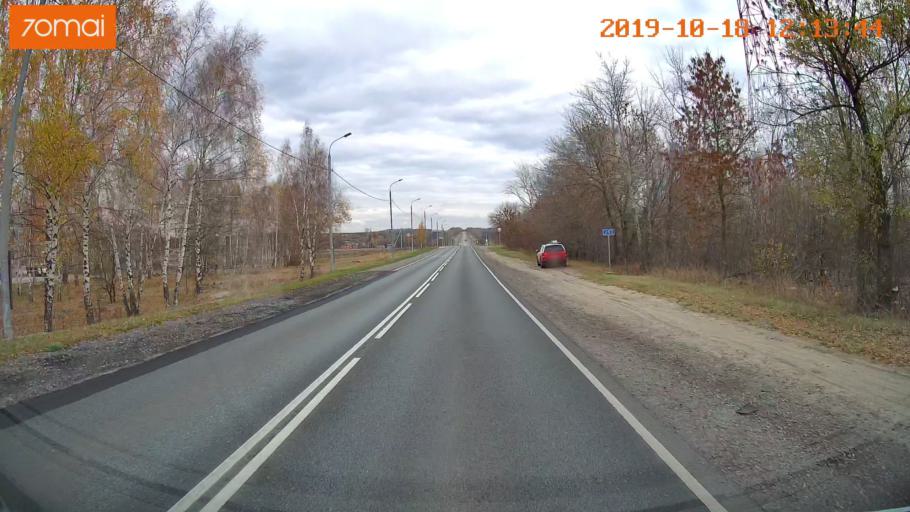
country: RU
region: Rjazan
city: Zakharovo
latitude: 54.4230
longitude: 39.3728
